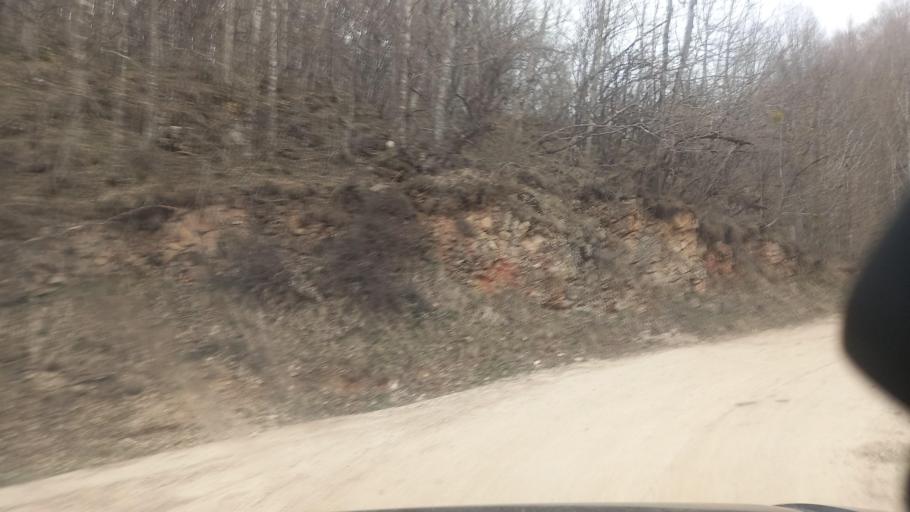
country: RU
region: Adygeya
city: Kamennomostskiy
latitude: 44.2074
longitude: 40.0025
